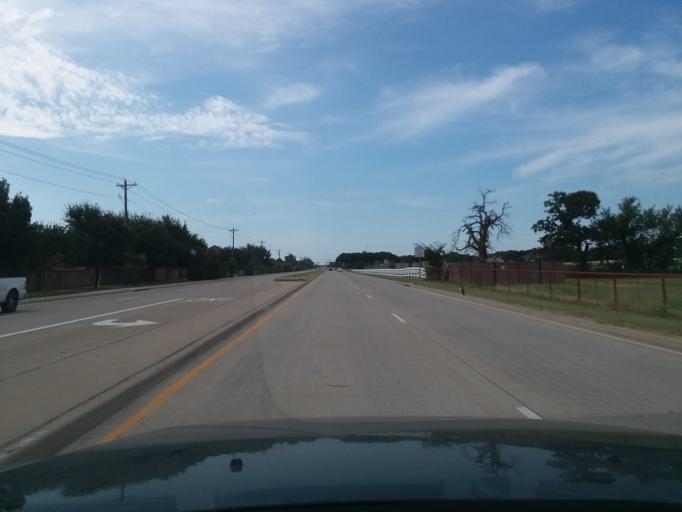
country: US
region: Texas
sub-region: Denton County
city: Bartonville
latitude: 33.0990
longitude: -97.1313
